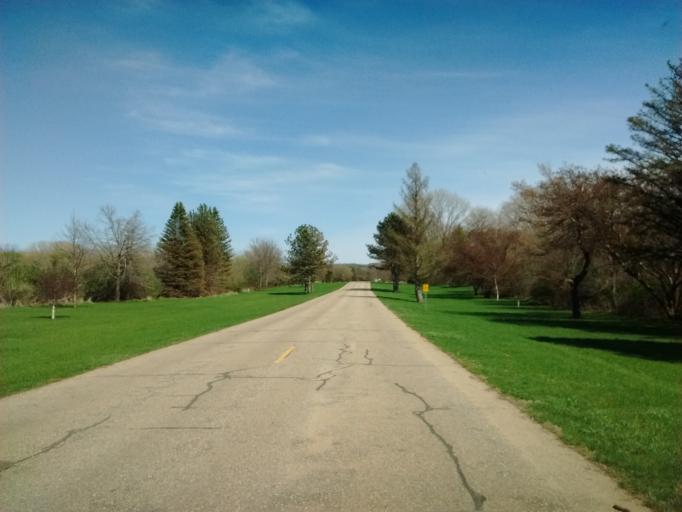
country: US
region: Iowa
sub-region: Plymouth County
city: Kingsley
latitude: 42.4514
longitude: -95.8045
